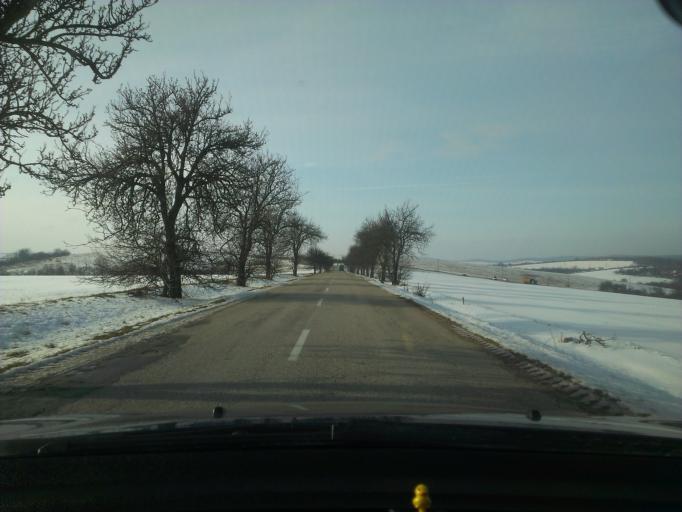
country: SK
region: Trenciansky
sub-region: Okres Myjava
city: Myjava
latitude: 48.7551
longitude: 17.6251
